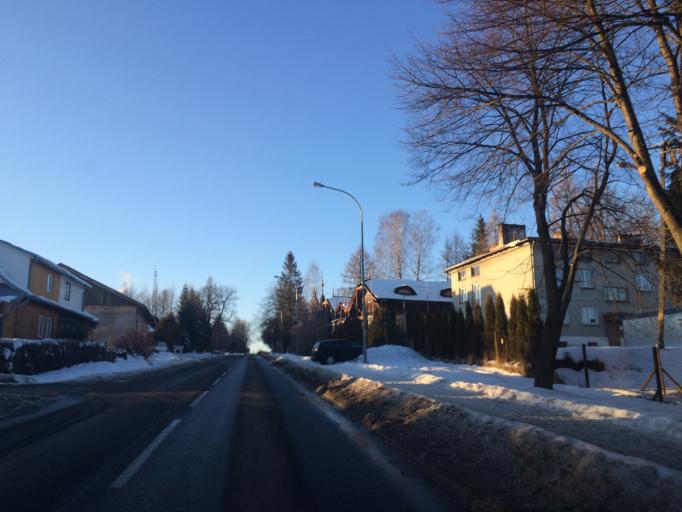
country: PL
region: Subcarpathian Voivodeship
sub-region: Powiat bieszczadzki
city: Lutowiska
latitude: 49.2518
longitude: 22.6944
